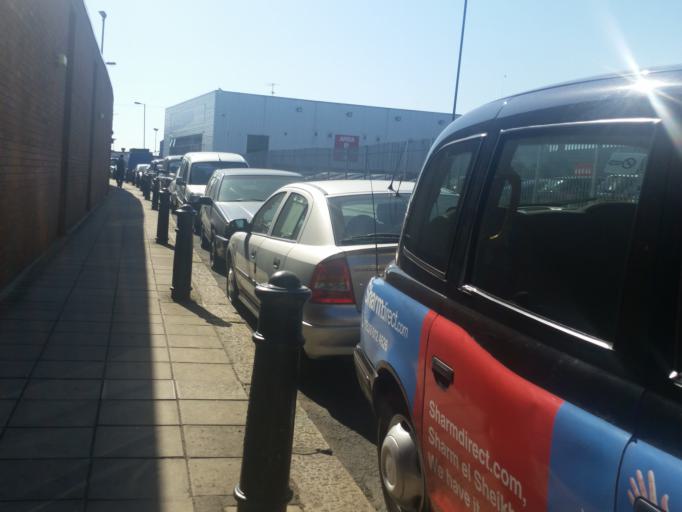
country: GB
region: England
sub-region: Greater London
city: Hammersmith
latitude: 51.5276
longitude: -0.2418
